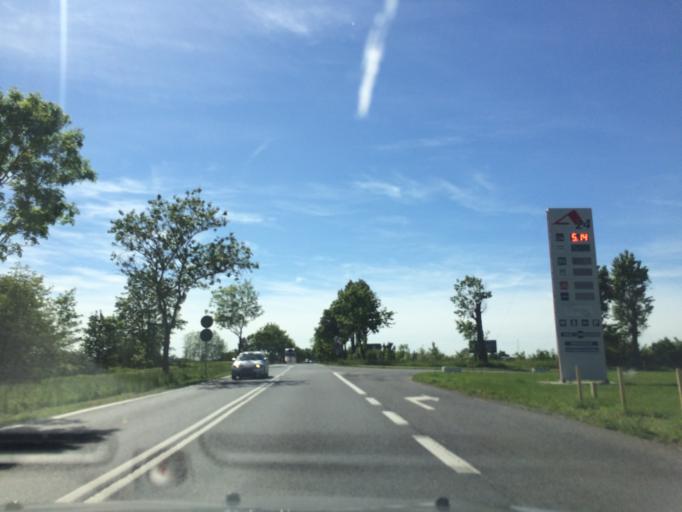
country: PL
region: Lower Silesian Voivodeship
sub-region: Powiat wroclawski
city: Sobotka
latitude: 50.9529
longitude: 16.7771
